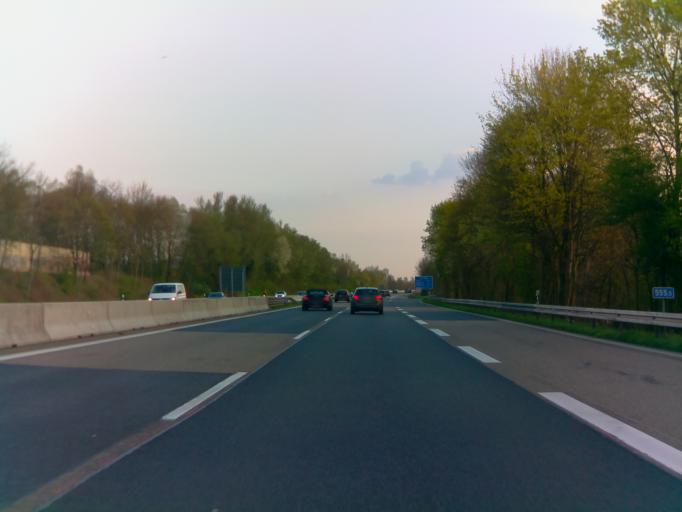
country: DE
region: Baden-Wuerttemberg
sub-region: Karlsruhe Region
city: Hemsbach
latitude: 49.5872
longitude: 8.6334
